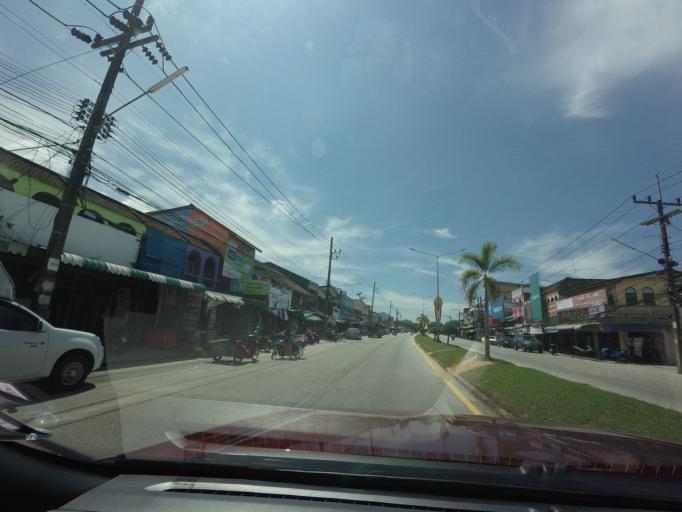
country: TH
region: Pattani
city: Mai Kaen
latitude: 6.6103
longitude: 101.6301
